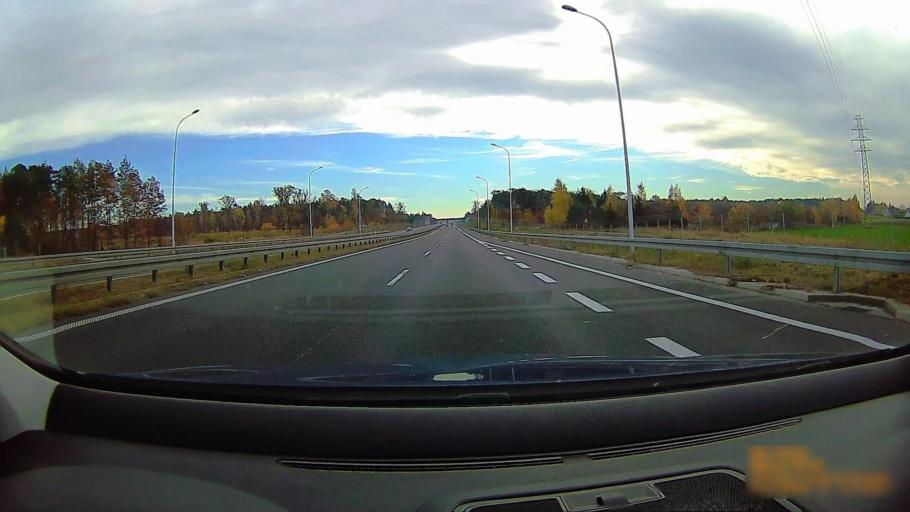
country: PL
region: Greater Poland Voivodeship
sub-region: Powiat ostrowski
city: Ostrow Wielkopolski
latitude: 51.6606
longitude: 17.8604
